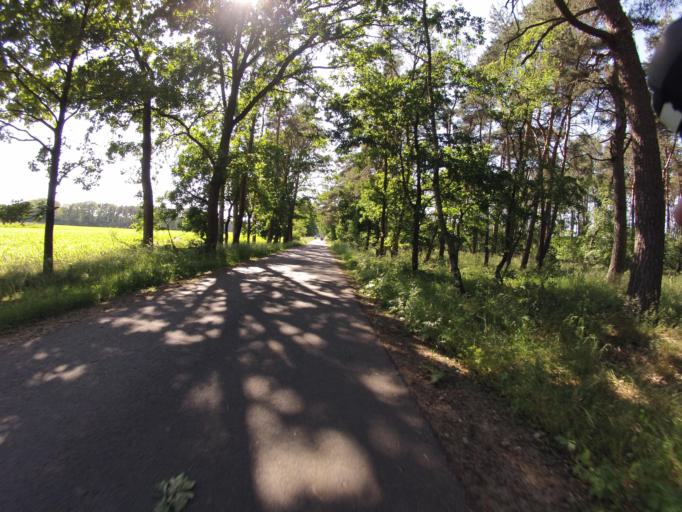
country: DE
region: North Rhine-Westphalia
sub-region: Regierungsbezirk Munster
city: Dreierwalde
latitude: 52.2601
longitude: 7.5284
